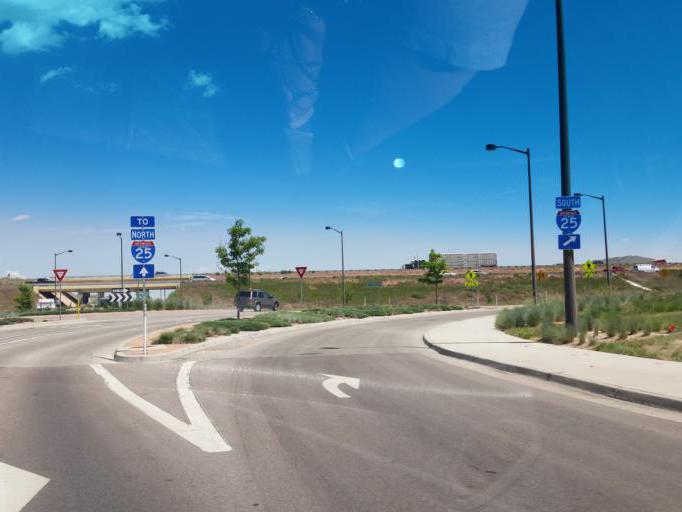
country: US
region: Colorado
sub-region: Larimer County
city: Loveland
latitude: 40.4359
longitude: -104.9942
